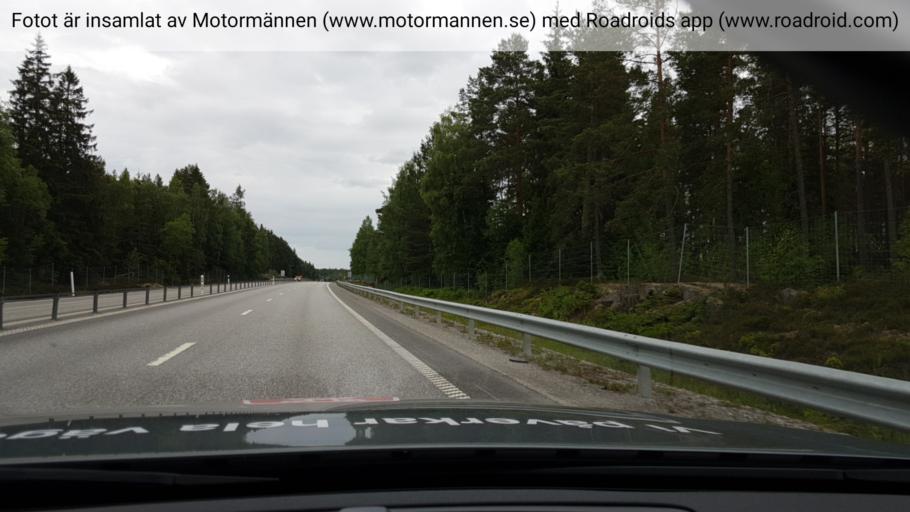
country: SE
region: Vaestmanland
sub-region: Surahammars Kommun
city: Surahammar
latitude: 59.7067
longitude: 16.2465
